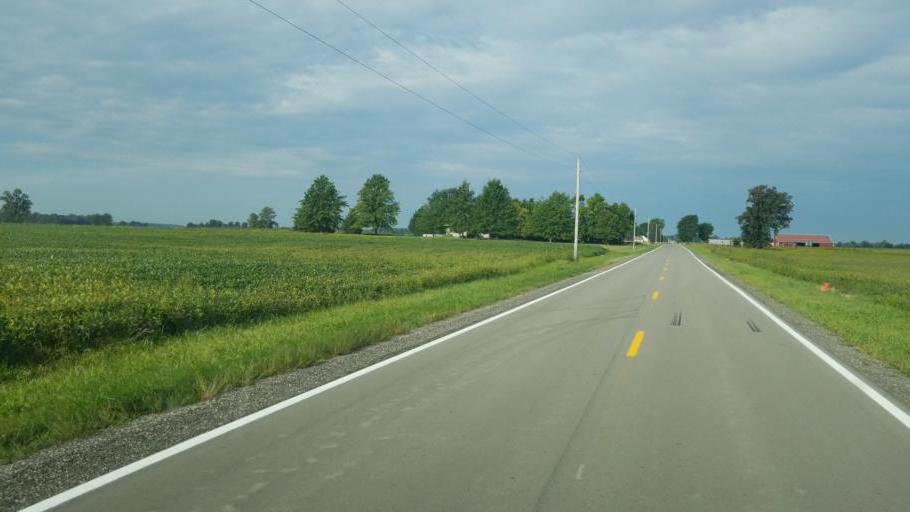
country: US
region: Ohio
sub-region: Marion County
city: Marion
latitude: 40.7174
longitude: -83.0992
